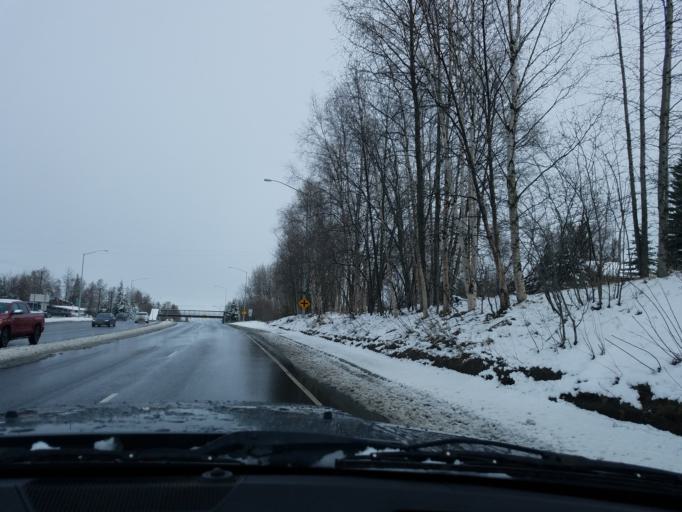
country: US
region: Alaska
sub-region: Anchorage Municipality
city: Anchorage
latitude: 61.1805
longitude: -149.9091
